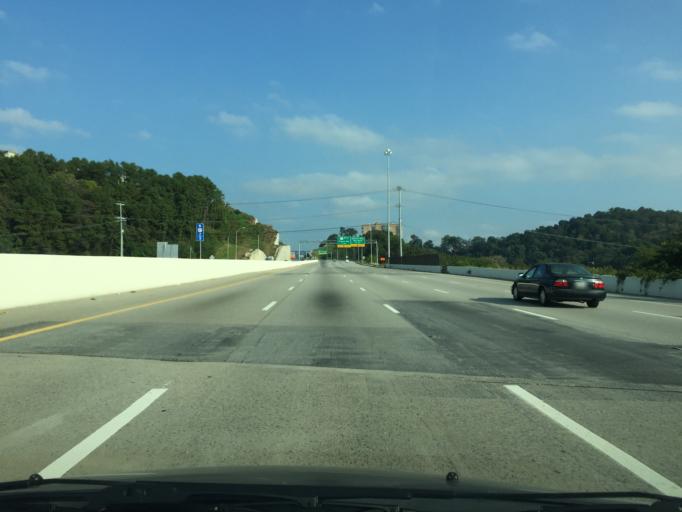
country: US
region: Tennessee
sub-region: Hamilton County
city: Chattanooga
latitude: 35.0649
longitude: -85.3184
